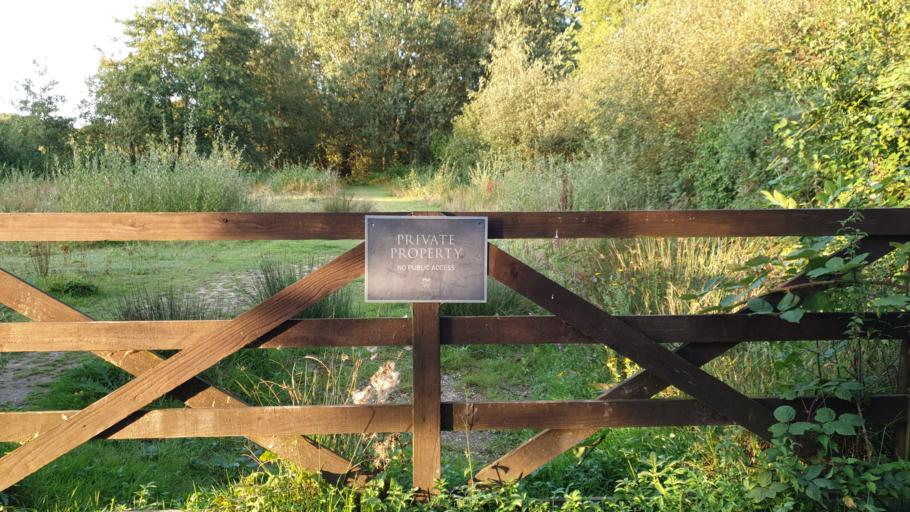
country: GB
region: England
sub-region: Wiltshire
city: Minety
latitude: 51.6478
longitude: -1.9651
